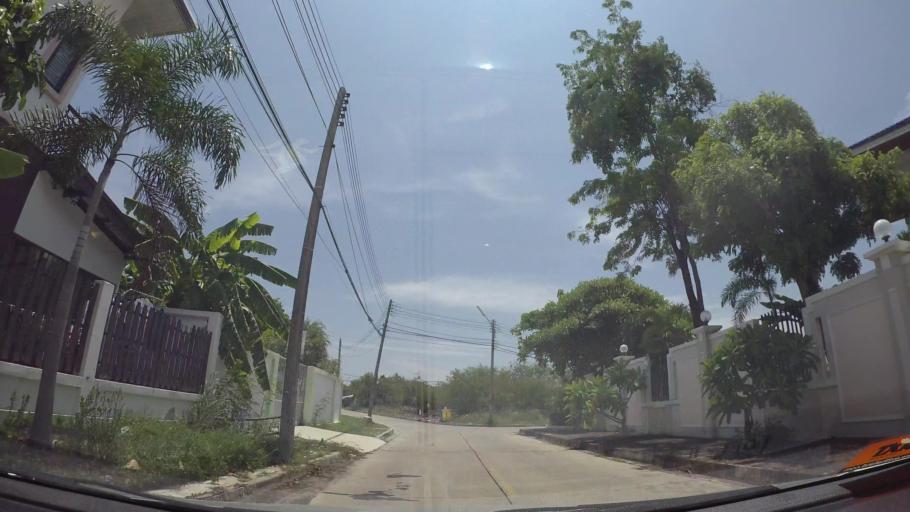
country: TH
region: Chon Buri
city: Chon Buri
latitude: 13.3345
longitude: 100.9427
